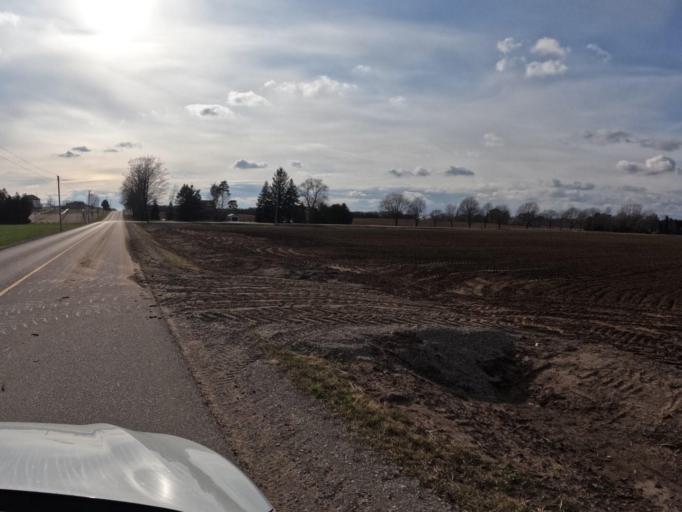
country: CA
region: Ontario
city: Brant
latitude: 43.0085
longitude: -80.3902
